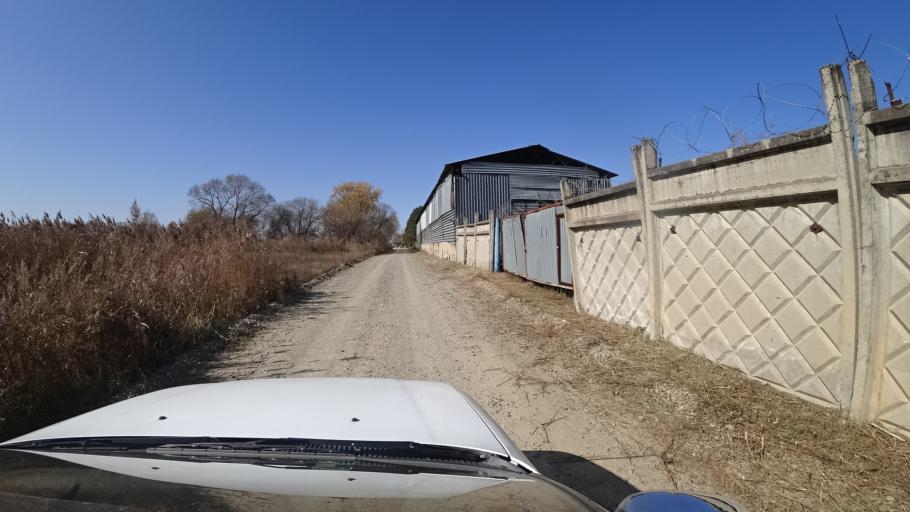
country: RU
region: Primorskiy
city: Dal'nerechensk
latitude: 45.9218
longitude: 133.7811
